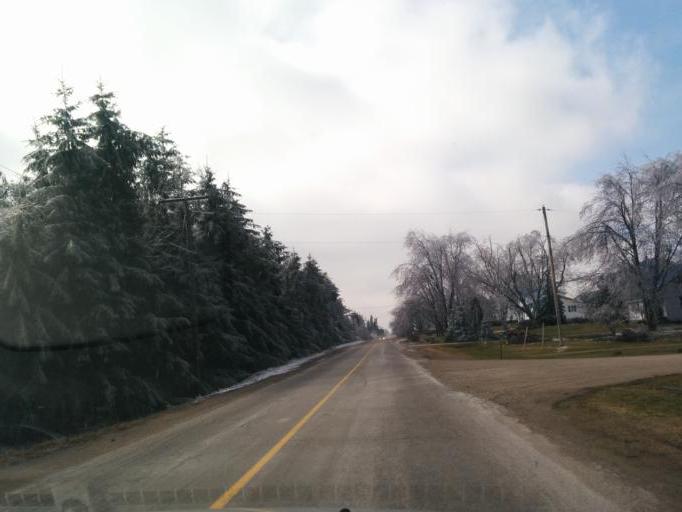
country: CA
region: Ontario
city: Waterloo
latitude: 43.6338
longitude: -80.5594
